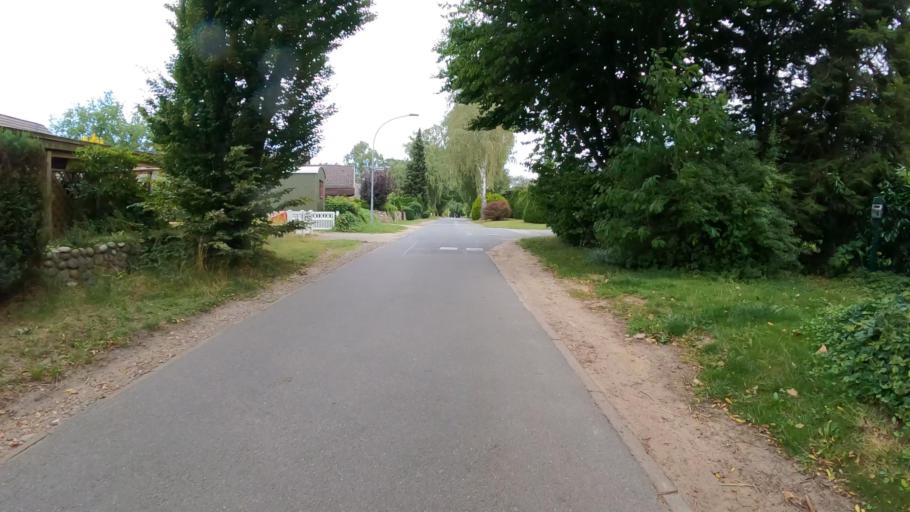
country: DE
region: Lower Saxony
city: Bendestorf
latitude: 53.3498
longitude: 9.9201
